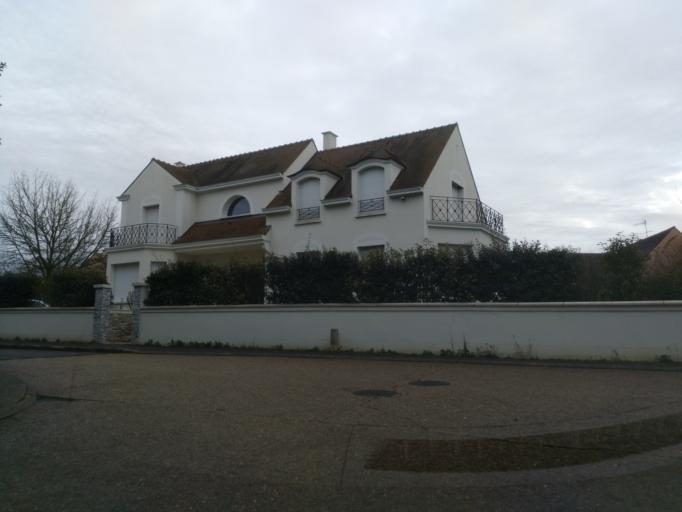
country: FR
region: Ile-de-France
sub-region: Departement des Yvelines
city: Saint-Nom-la-Breteche
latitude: 48.8691
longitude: 2.0070
